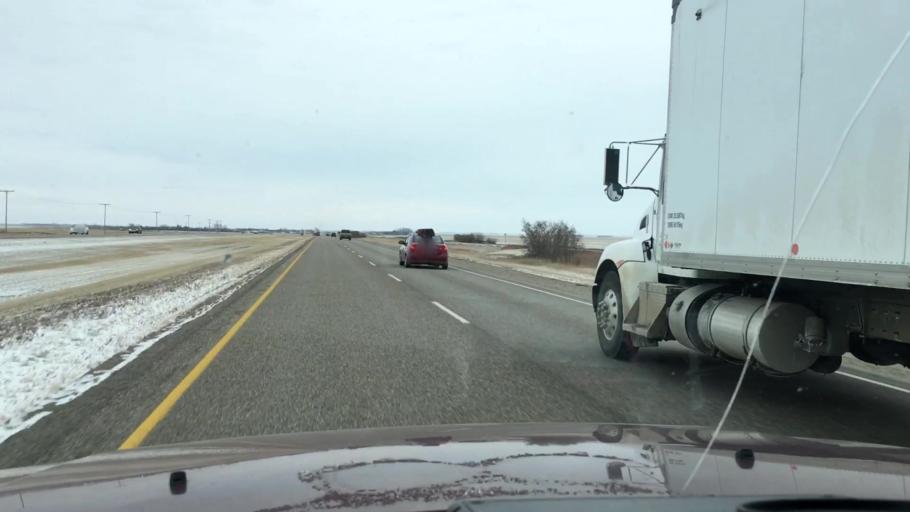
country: CA
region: Saskatchewan
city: Watrous
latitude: 51.1773
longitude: -105.9364
